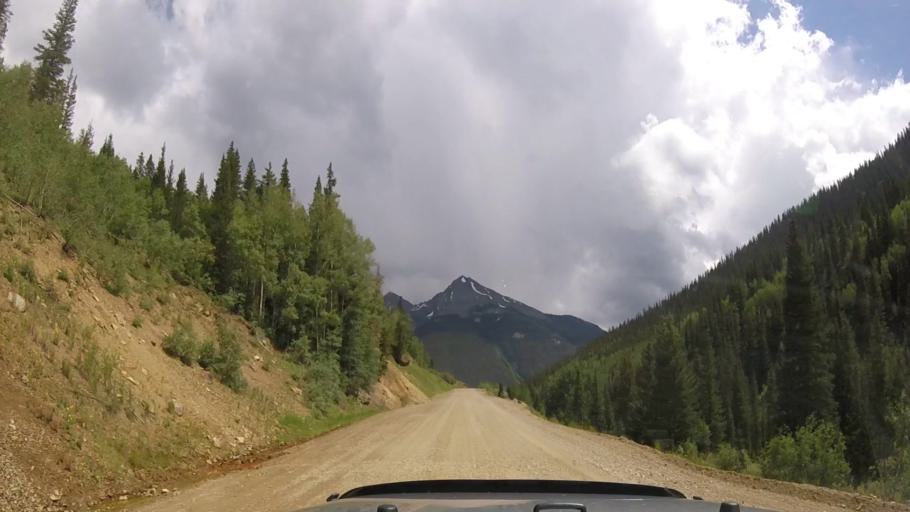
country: US
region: Colorado
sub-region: San Juan County
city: Silverton
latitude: 37.8249
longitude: -107.6669
